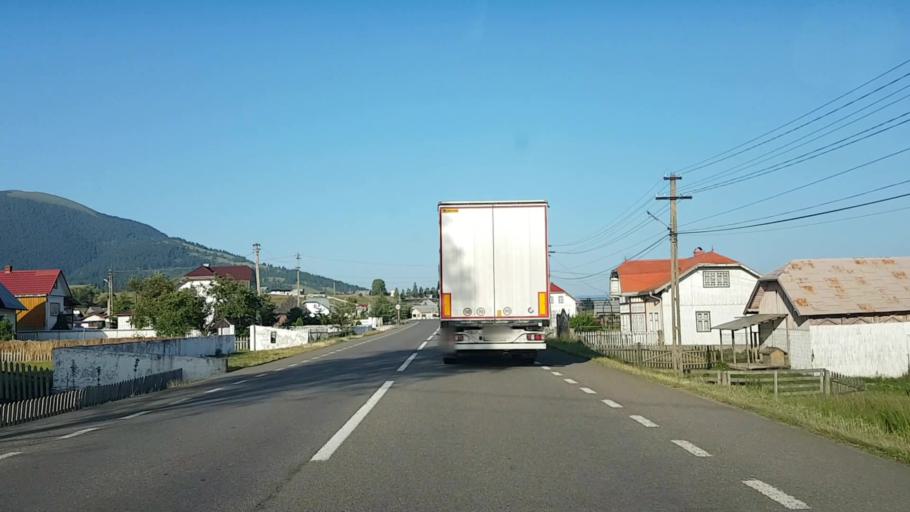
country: RO
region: Suceava
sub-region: Comuna Cosna
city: Cosna
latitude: 47.3608
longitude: 25.1993
